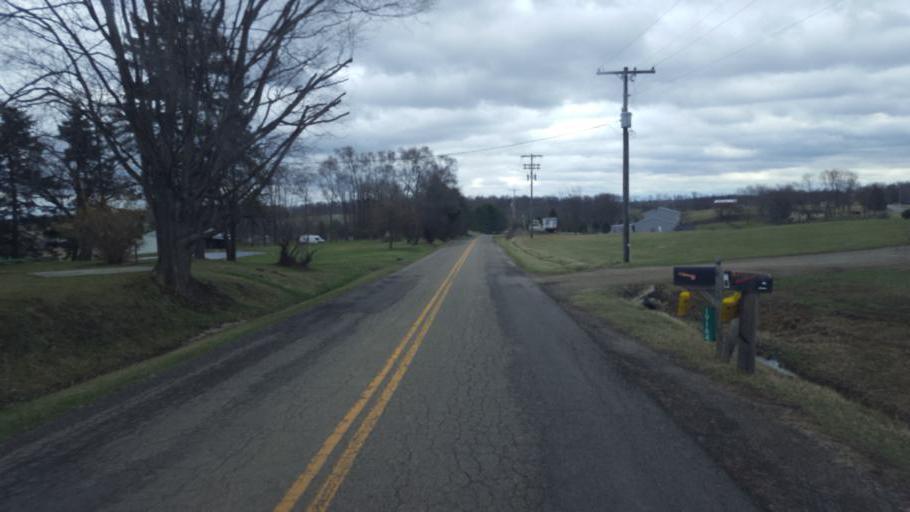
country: US
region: Ohio
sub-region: Licking County
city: Utica
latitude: 40.2434
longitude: -82.4167
